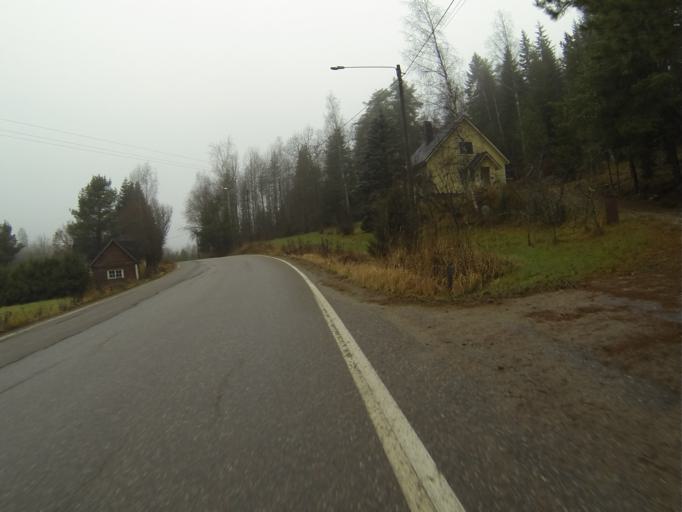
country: FI
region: Varsinais-Suomi
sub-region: Salo
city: Halikko
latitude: 60.4171
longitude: 22.9216
